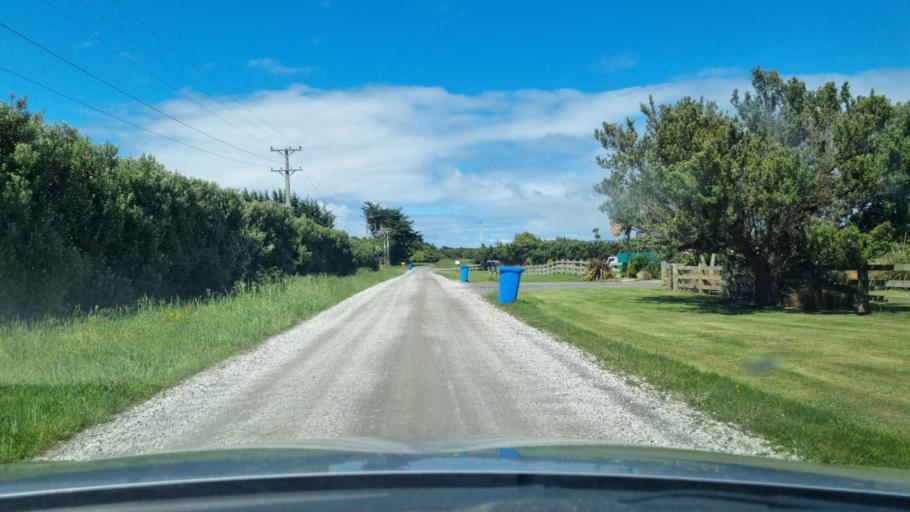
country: NZ
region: Southland
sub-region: Invercargill City
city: Invercargill
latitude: -46.4432
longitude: 168.2784
